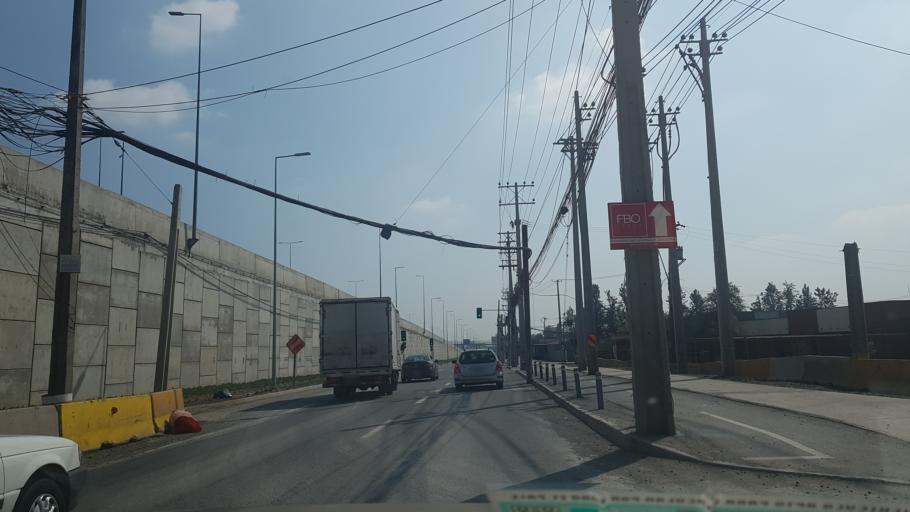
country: CL
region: Santiago Metropolitan
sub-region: Provincia de Chacabuco
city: Chicureo Abajo
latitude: -33.3461
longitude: -70.7089
